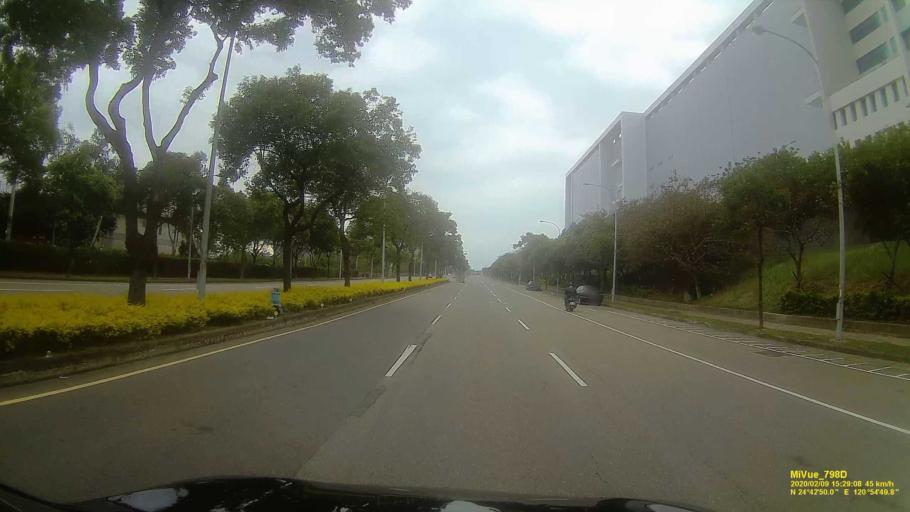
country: TW
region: Taiwan
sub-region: Hsinchu
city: Hsinchu
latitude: 24.7139
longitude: 120.9136
